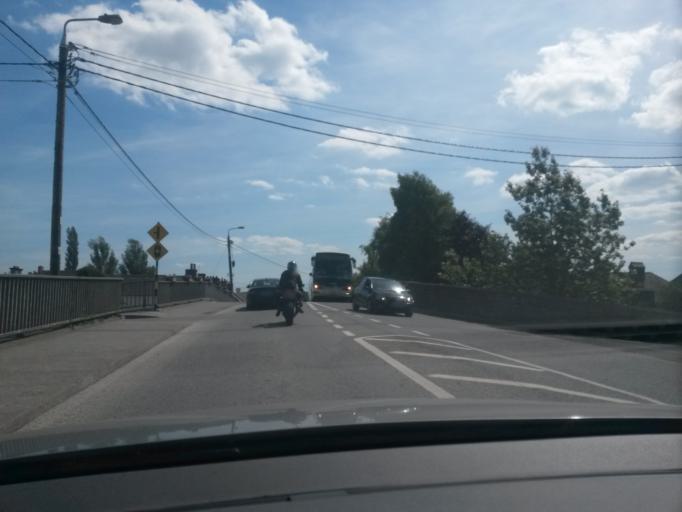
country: IE
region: Leinster
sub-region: Kildare
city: Sallins
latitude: 53.2495
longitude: -6.6653
